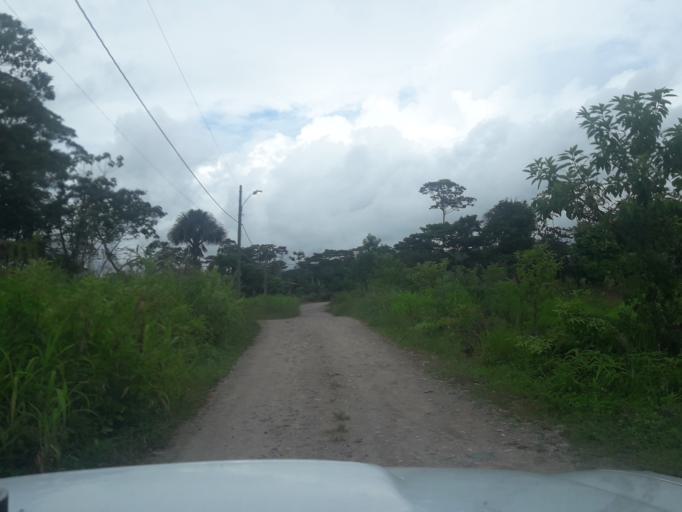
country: EC
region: Napo
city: Archidona
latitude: -0.9515
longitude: -77.8118
